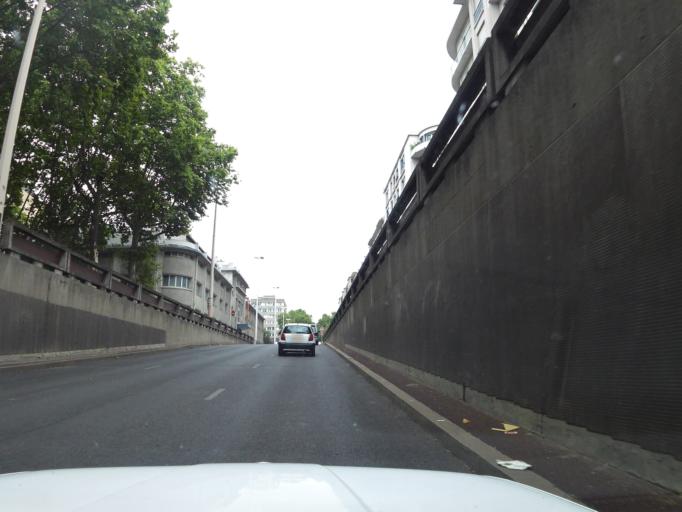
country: FR
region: Rhone-Alpes
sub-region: Departement du Rhone
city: Lyon
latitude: 45.7566
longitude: 4.8528
